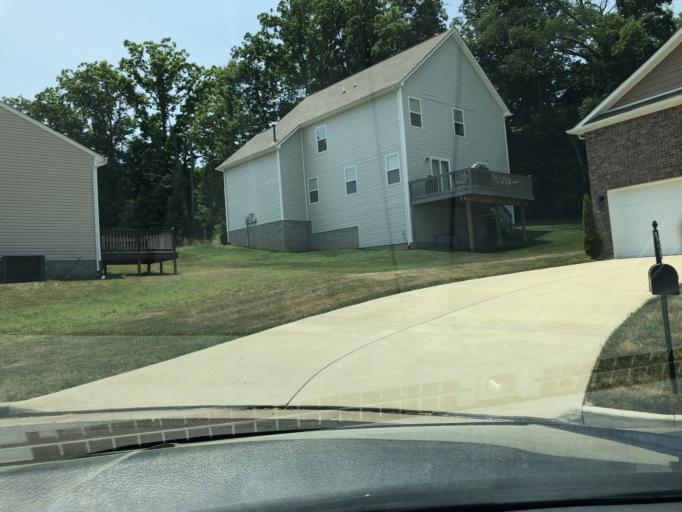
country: US
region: Tennessee
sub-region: Rutherford County
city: La Vergne
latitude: 36.0494
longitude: -86.6219
